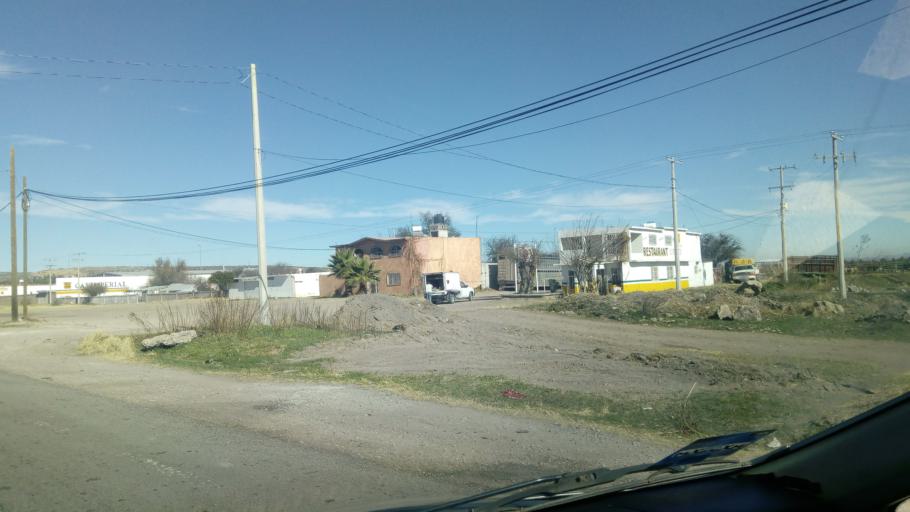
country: MX
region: Durango
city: Victoria de Durango
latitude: 24.0918
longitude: -104.5710
